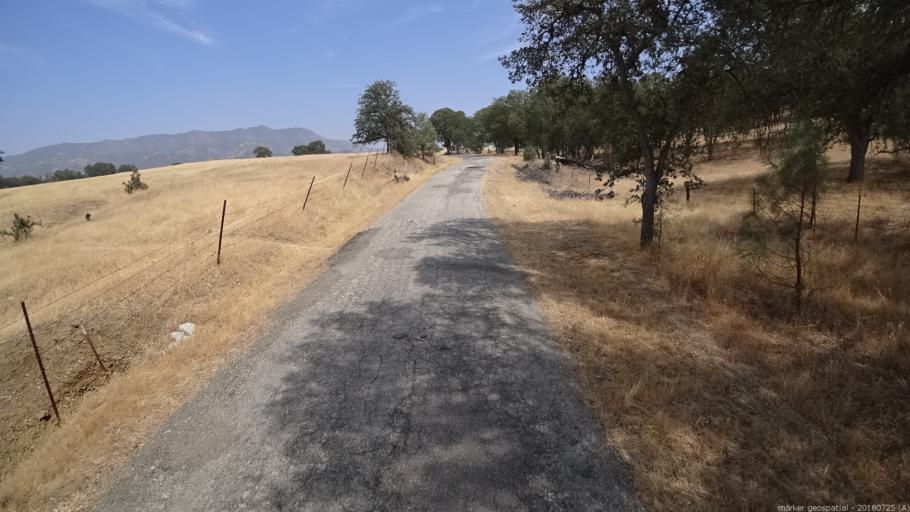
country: US
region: California
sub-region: Fresno County
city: Coalinga
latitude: 36.1834
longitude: -120.6703
